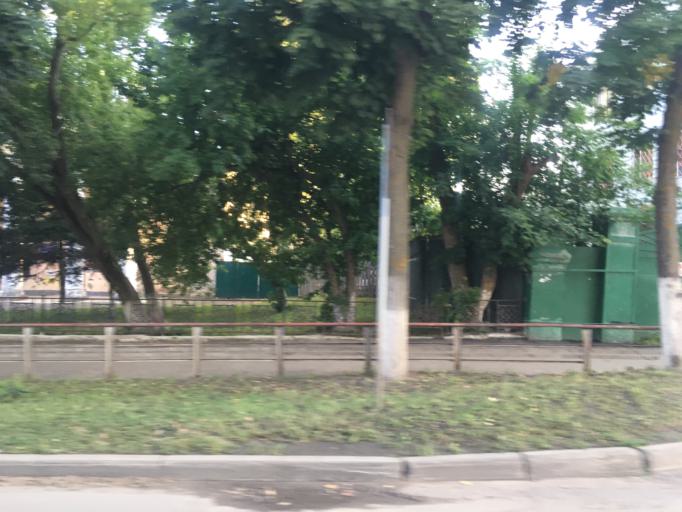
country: RU
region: Mariy-El
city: Yoshkar-Ola
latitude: 56.6460
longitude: 47.8905
